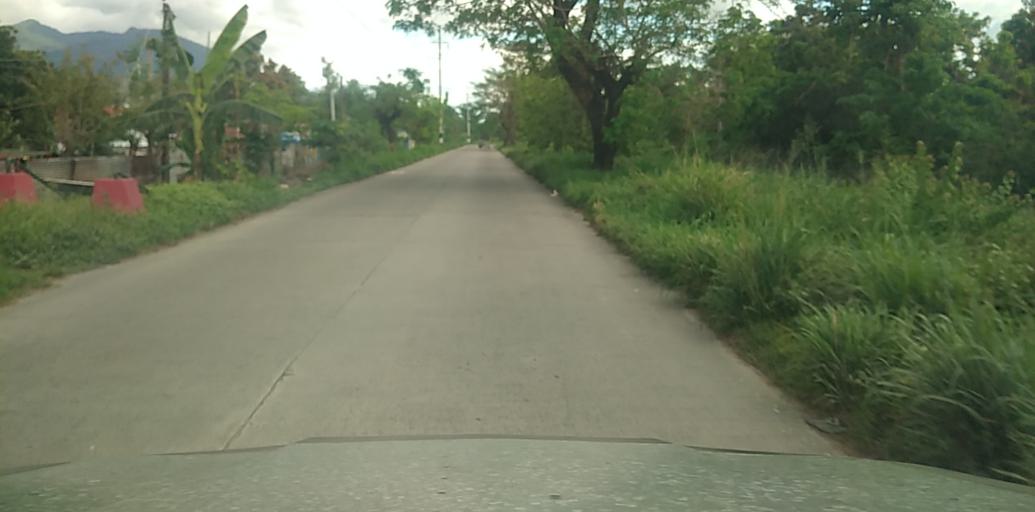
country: PH
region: Central Luzon
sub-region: Province of Pampanga
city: Pandacaqui
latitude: 15.1771
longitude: 120.6646
